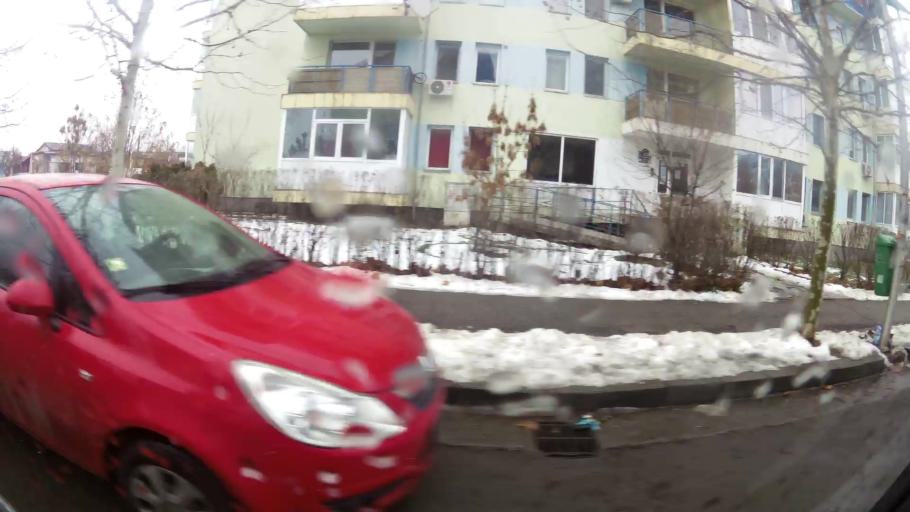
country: RO
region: Ilfov
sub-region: Comuna Chiajna
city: Rosu
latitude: 44.4203
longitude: 26.0099
